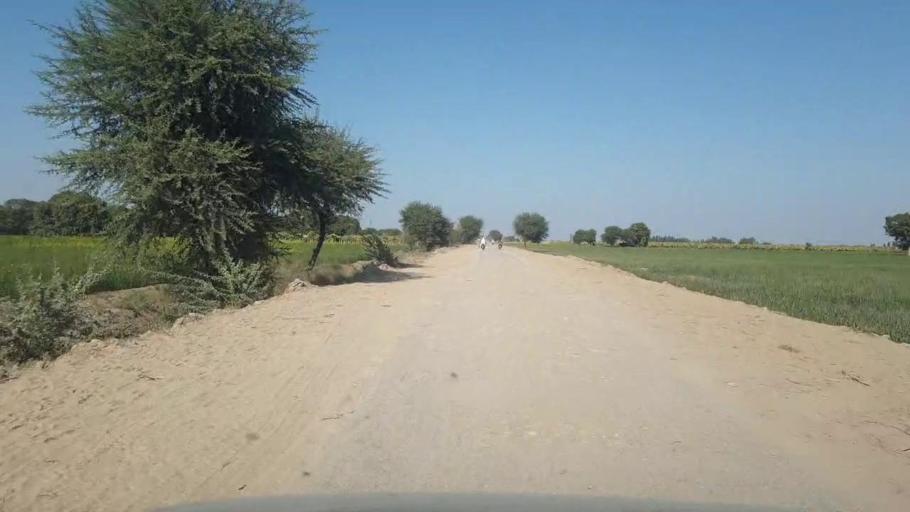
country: PK
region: Sindh
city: Samaro
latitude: 25.3415
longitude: 69.3095
